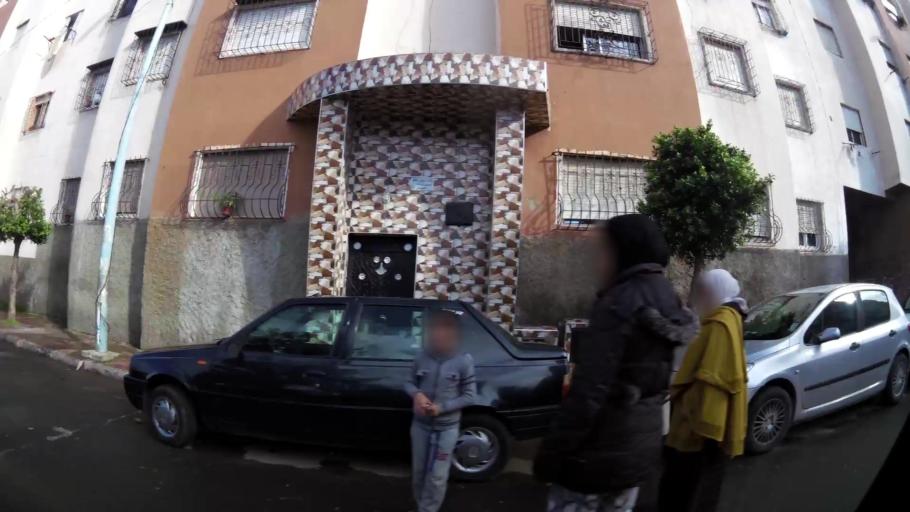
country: MA
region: Grand Casablanca
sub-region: Casablanca
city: Casablanca
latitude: 33.5560
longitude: -7.6983
